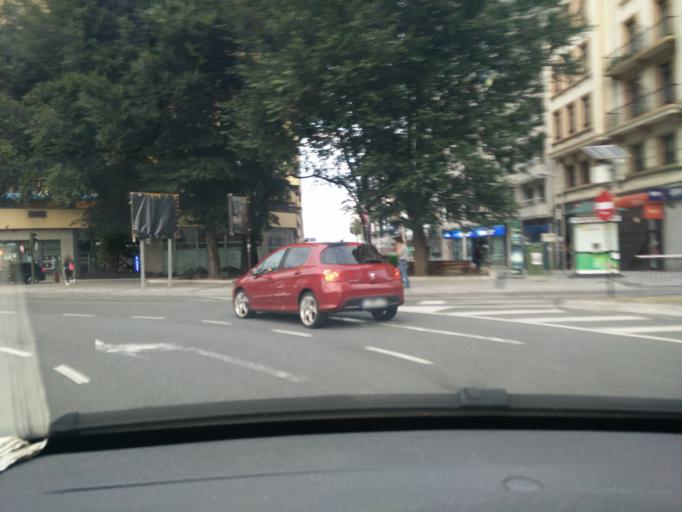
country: ES
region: Galicia
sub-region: Provincia da Coruna
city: A Coruna
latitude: 43.3570
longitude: -8.4040
